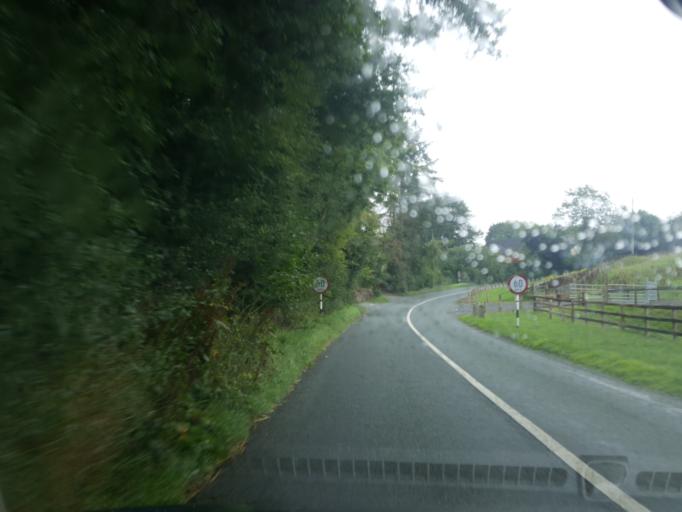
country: IE
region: Leinster
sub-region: Wicklow
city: Valleymount
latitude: 53.1278
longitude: -6.5843
